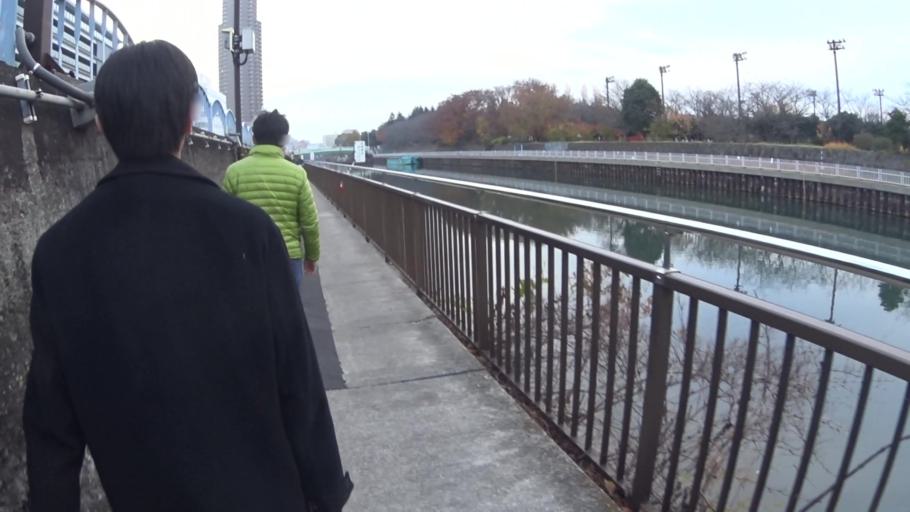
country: JP
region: Tokyo
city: Urayasu
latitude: 35.6915
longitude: 139.8206
